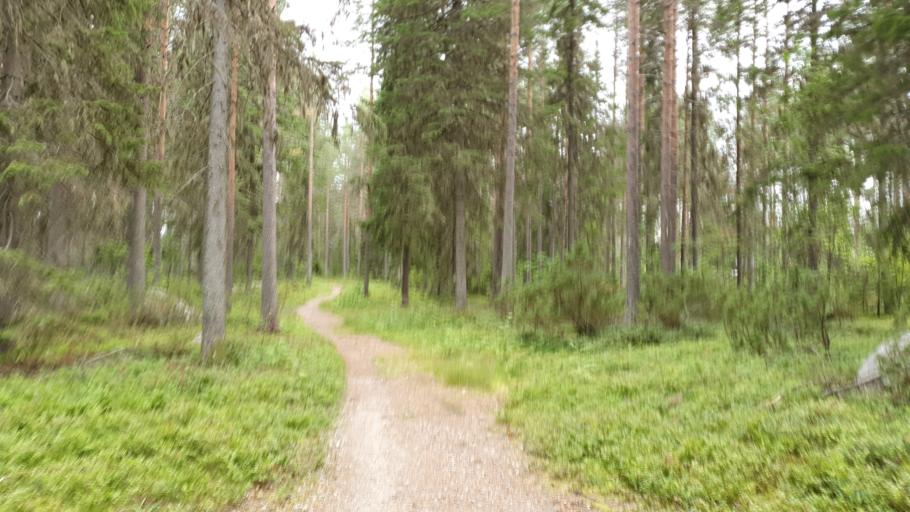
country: FI
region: Kainuu
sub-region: Kehys-Kainuu
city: Kuhmo
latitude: 64.1351
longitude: 29.4662
